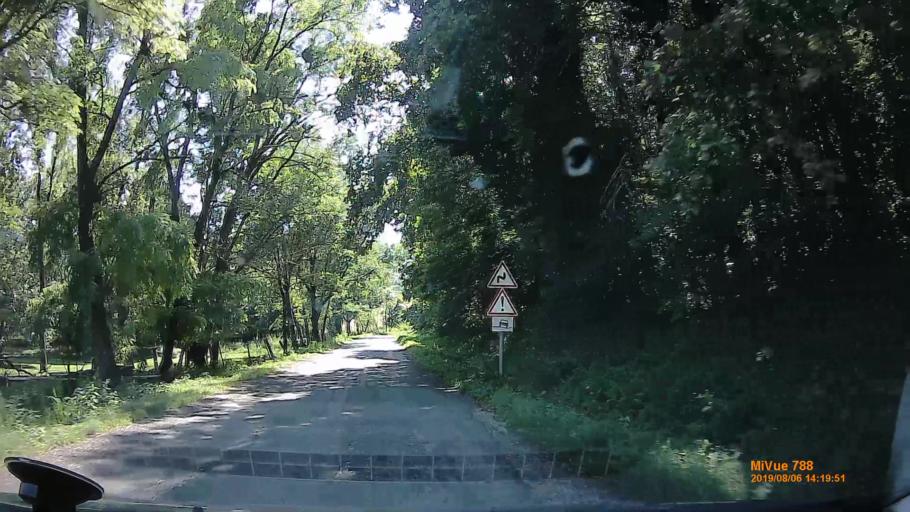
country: HU
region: Zala
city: Zalakomar
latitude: 46.5274
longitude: 17.0894
